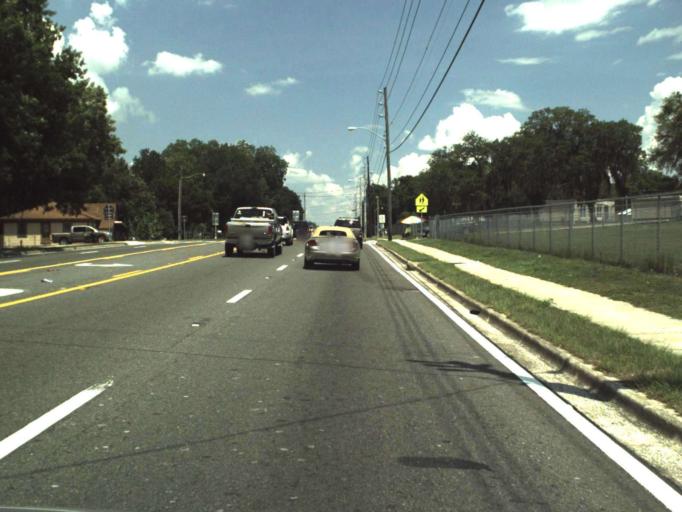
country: US
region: Florida
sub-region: Lake County
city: Leesburg
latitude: 28.8030
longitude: -81.8981
